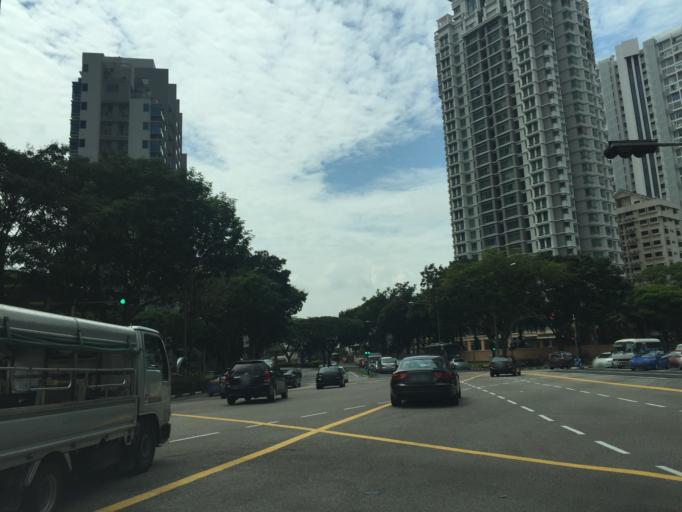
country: SG
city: Singapore
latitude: 1.3190
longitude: 103.8435
